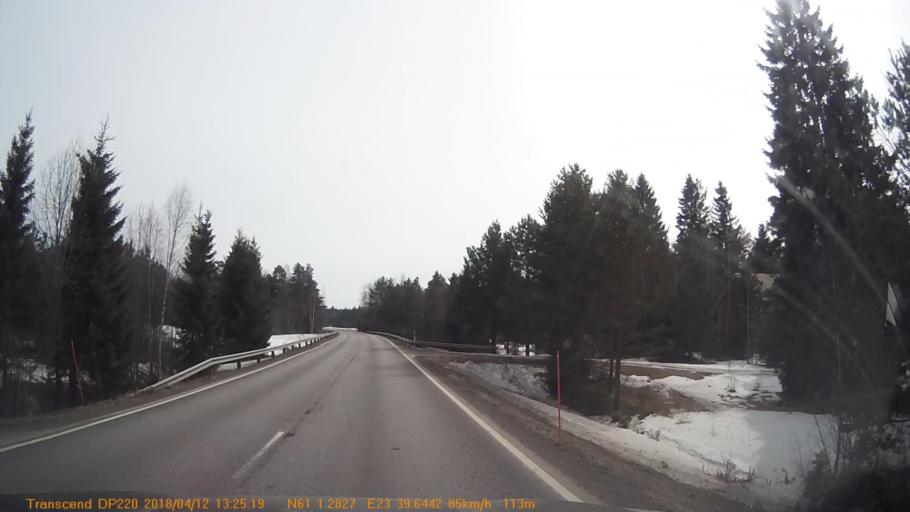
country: FI
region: Pirkanmaa
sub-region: Etelae-Pirkanmaa
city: Kylmaekoski
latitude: 61.0212
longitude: 23.6609
